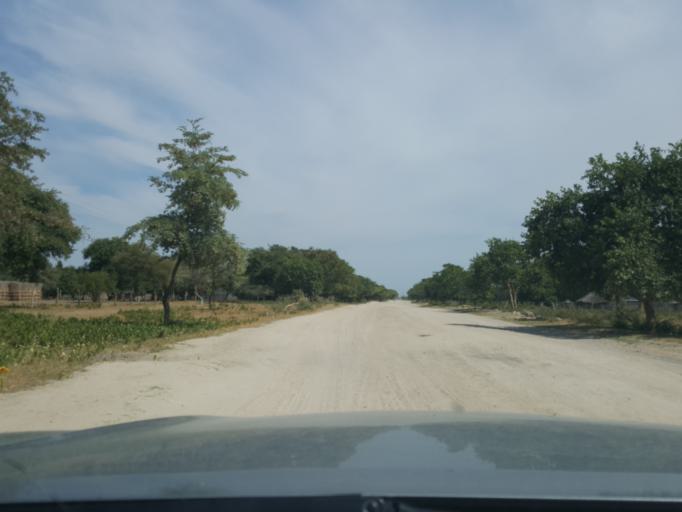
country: BW
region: North West
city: Shakawe
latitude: -18.3127
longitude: 21.8975
